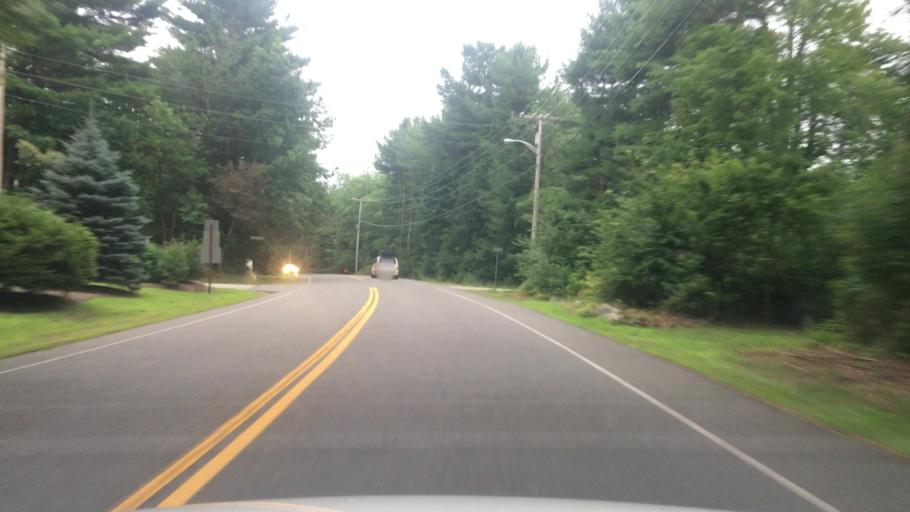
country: US
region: Maine
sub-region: York County
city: Wells Beach Station
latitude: 43.3196
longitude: -70.6008
